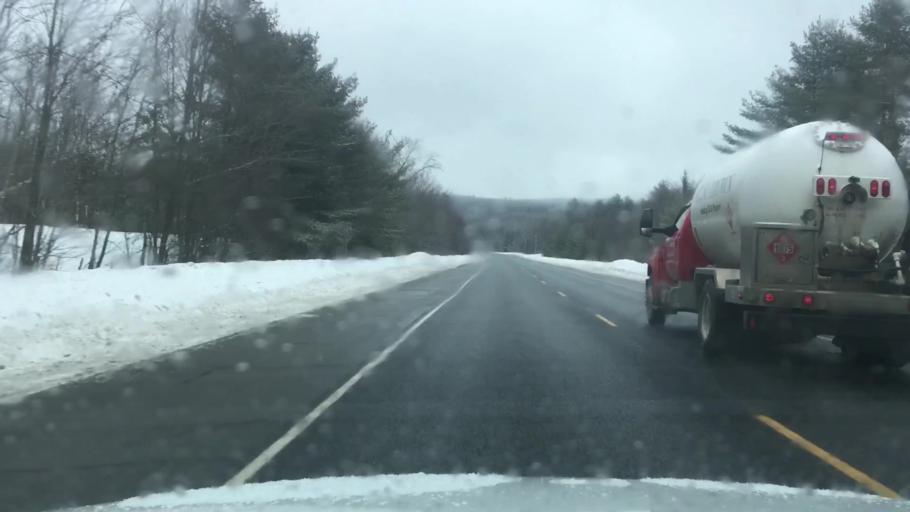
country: US
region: Maine
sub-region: Franklin County
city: Wilton
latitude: 44.5741
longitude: -70.2938
